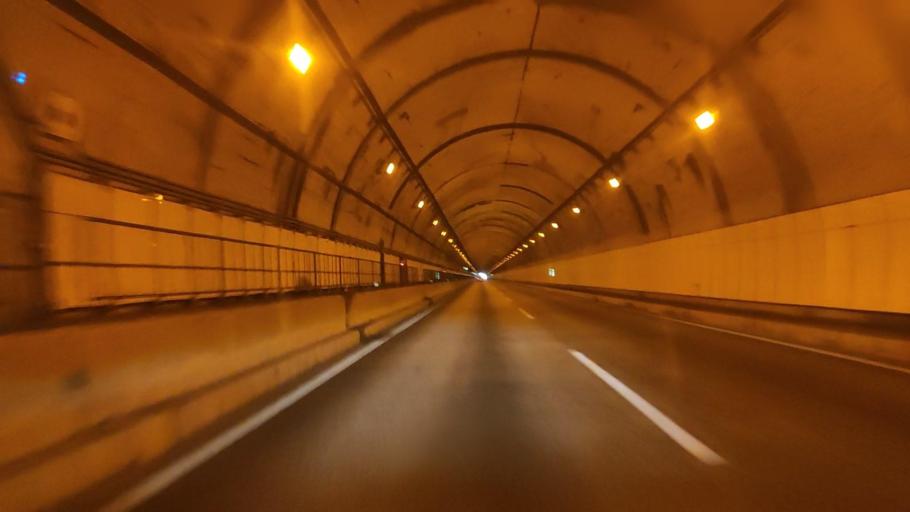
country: JP
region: Miyazaki
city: Miyakonojo
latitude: 31.8235
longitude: 131.2353
